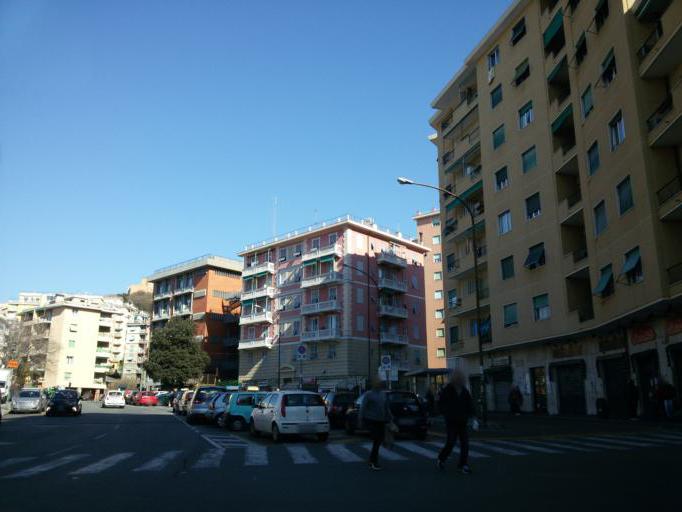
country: IT
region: Liguria
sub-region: Provincia di Genova
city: San Teodoro
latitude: 44.4190
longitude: 8.9151
